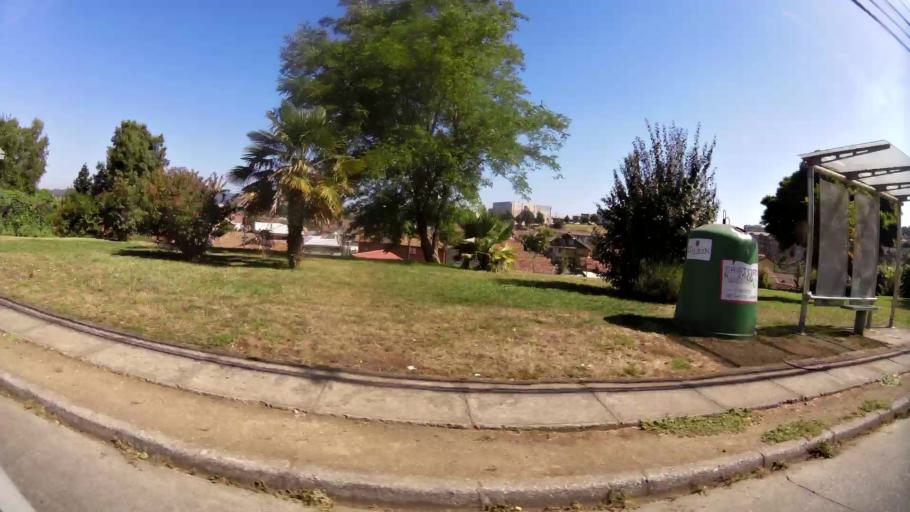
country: CL
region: Biobio
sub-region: Provincia de Concepcion
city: Concepcion
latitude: -36.7951
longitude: -73.0532
